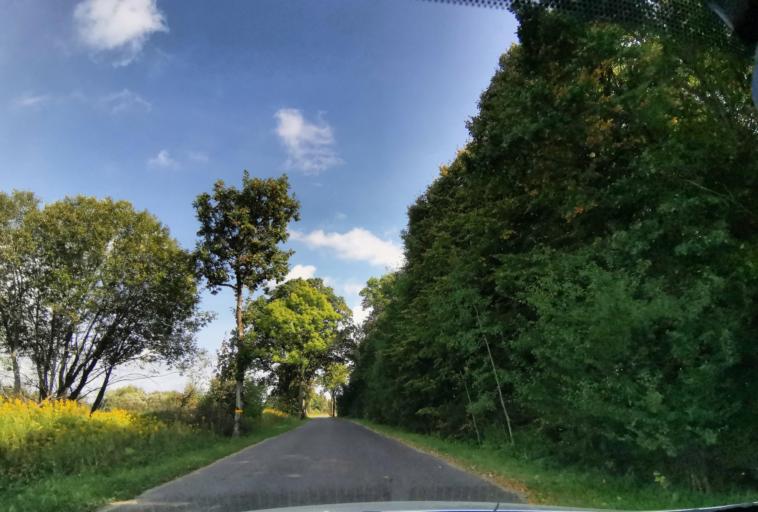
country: RU
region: Kaliningrad
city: Chernyakhovsk
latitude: 54.6580
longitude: 21.9086
